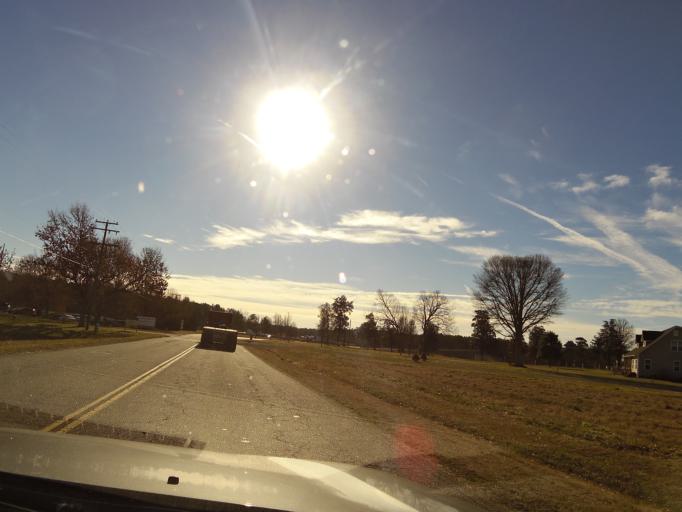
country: US
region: Virginia
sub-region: City of Petersburg
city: Petersburg
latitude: 37.1926
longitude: -77.4241
